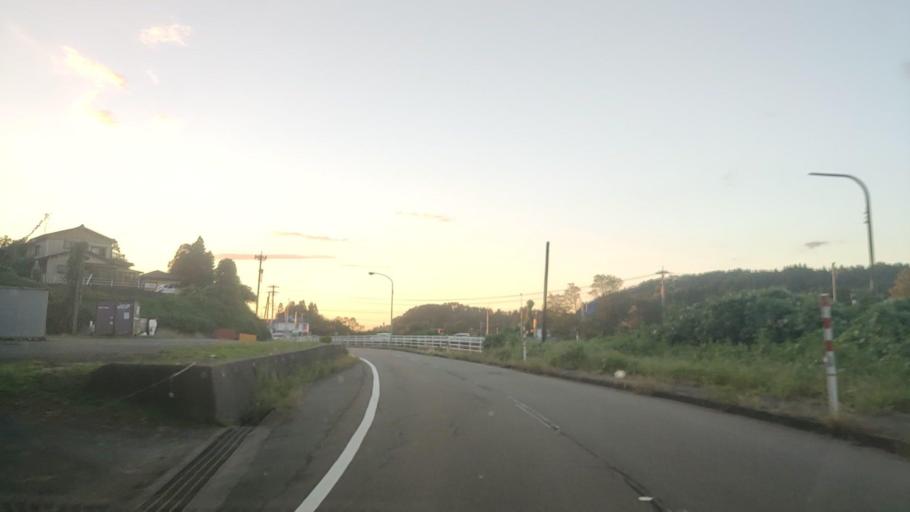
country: JP
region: Ishikawa
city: Tsubata
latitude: 36.6653
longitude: 136.7478
